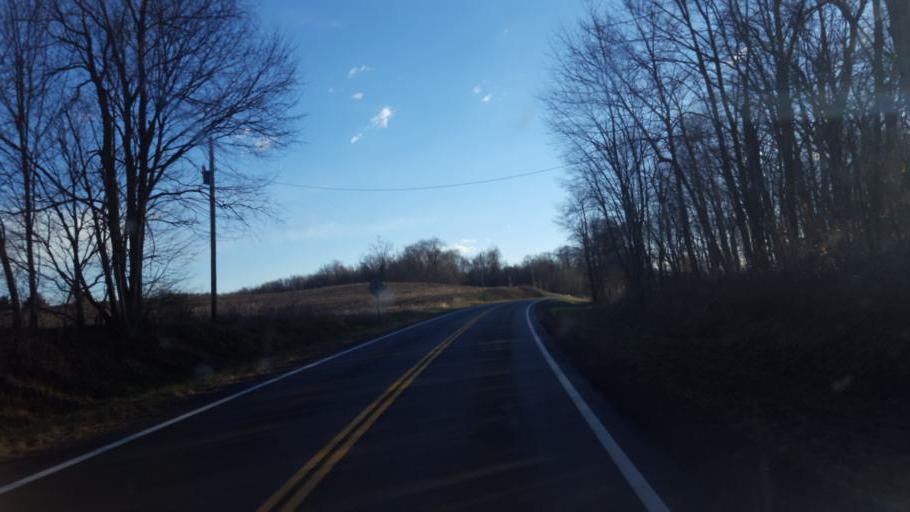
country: US
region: Ohio
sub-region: Sandusky County
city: Bellville
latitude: 40.6457
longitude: -82.3732
